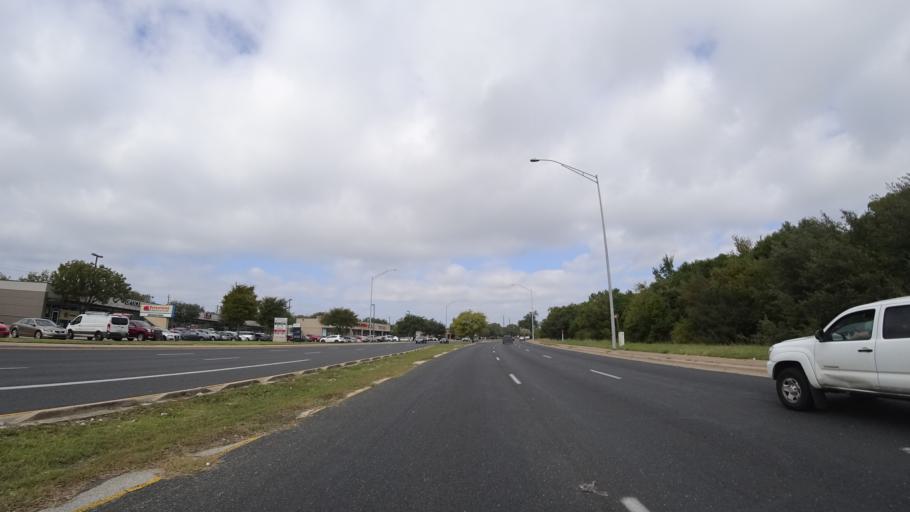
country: US
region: Texas
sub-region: Travis County
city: Shady Hollow
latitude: 30.2148
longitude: -97.8321
